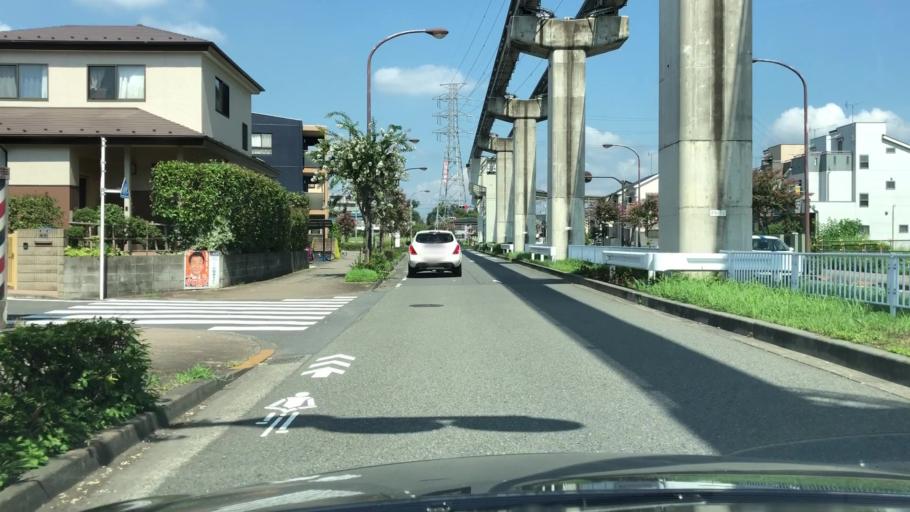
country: JP
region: Tokyo
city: Hino
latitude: 35.6793
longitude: 139.4074
